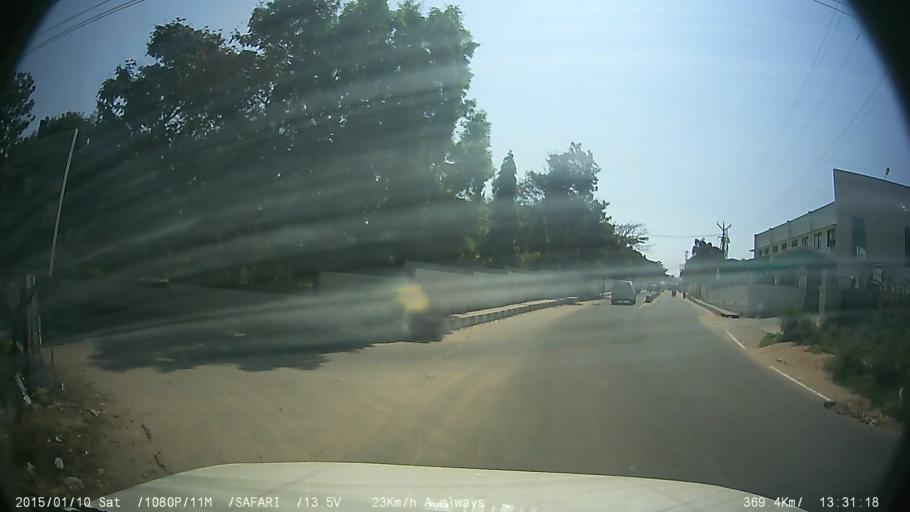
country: IN
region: Tamil Nadu
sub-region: Krishnagiri
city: Hosur
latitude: 12.7645
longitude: 77.7959
